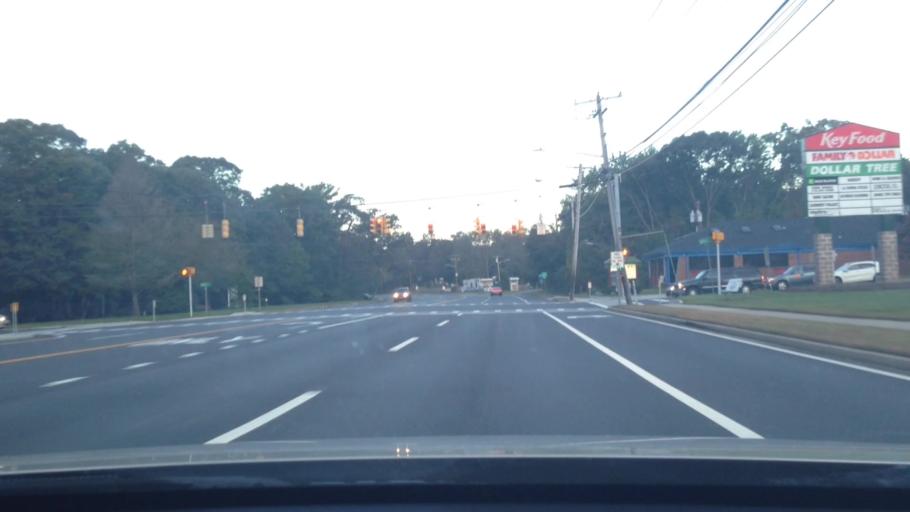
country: US
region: New York
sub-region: Suffolk County
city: Farmingville
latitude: 40.8358
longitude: -73.0475
